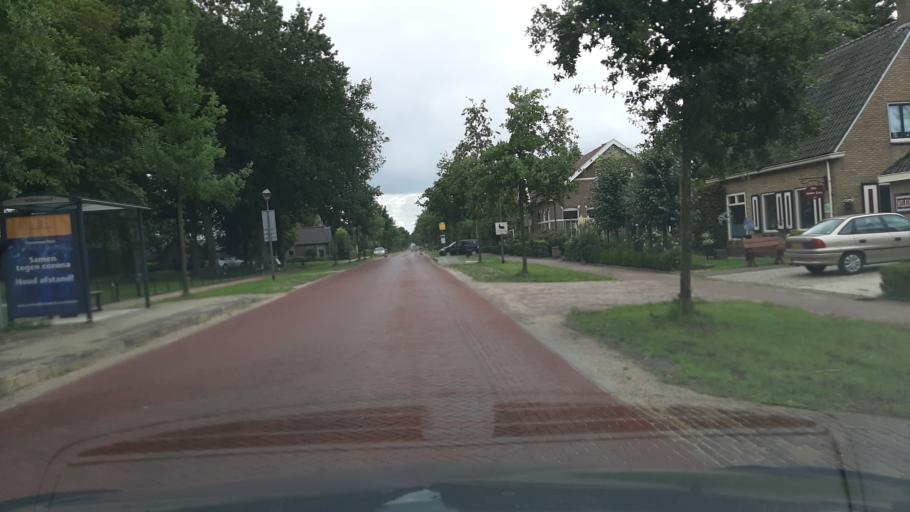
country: NL
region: Overijssel
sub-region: Gemeente Steenwijkerland
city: Steenwijkerwold
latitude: 52.8250
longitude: 6.0619
